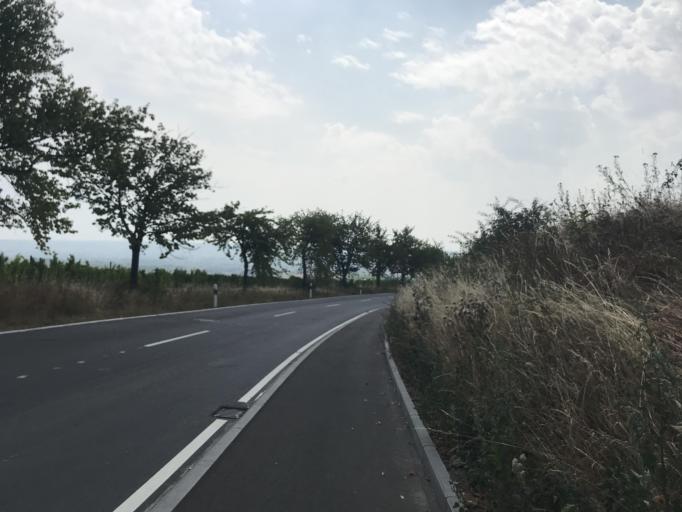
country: DE
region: Rheinland-Pfalz
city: Oestrich-Winkel
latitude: 50.0323
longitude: 8.0326
